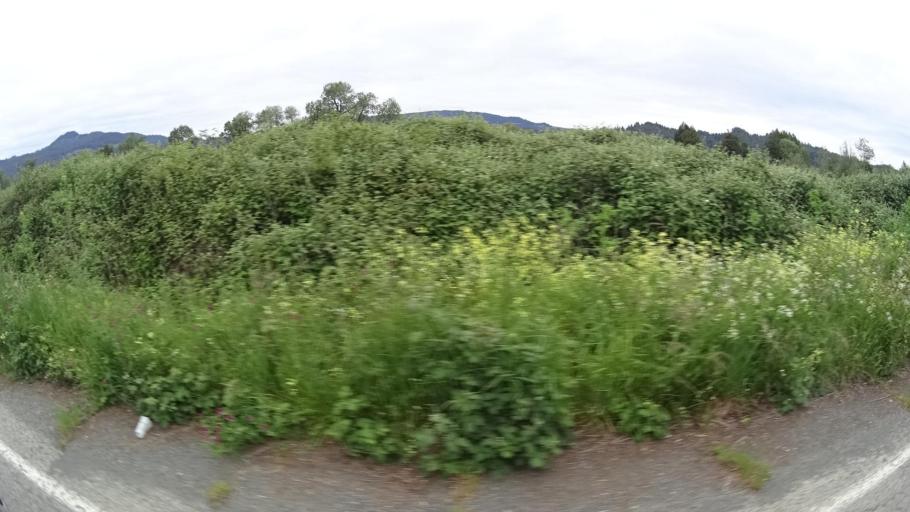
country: US
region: California
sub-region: Humboldt County
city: Blue Lake
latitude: 40.8656
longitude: -123.9957
